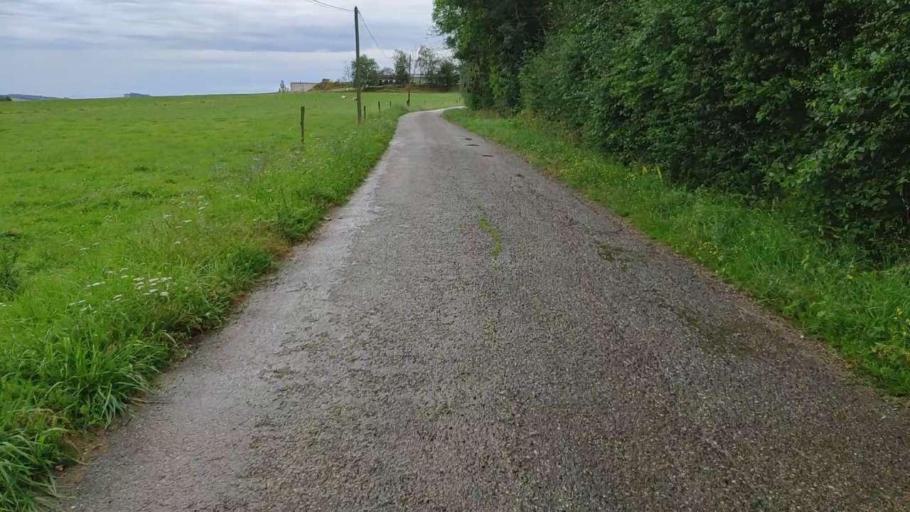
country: FR
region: Franche-Comte
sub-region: Departement du Jura
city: Poligny
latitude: 46.7868
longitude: 5.6047
